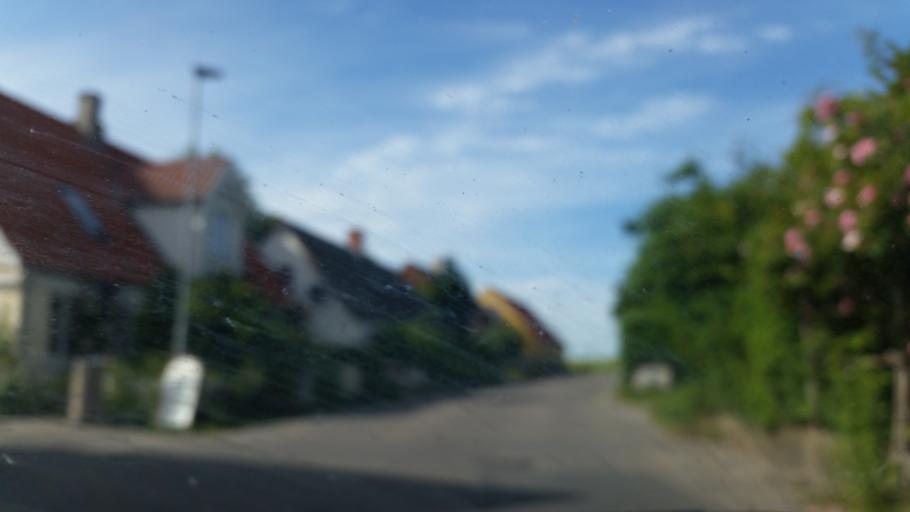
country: DK
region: Central Jutland
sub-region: Samso Kommune
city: Tranebjerg
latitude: 55.8274
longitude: 10.5609
